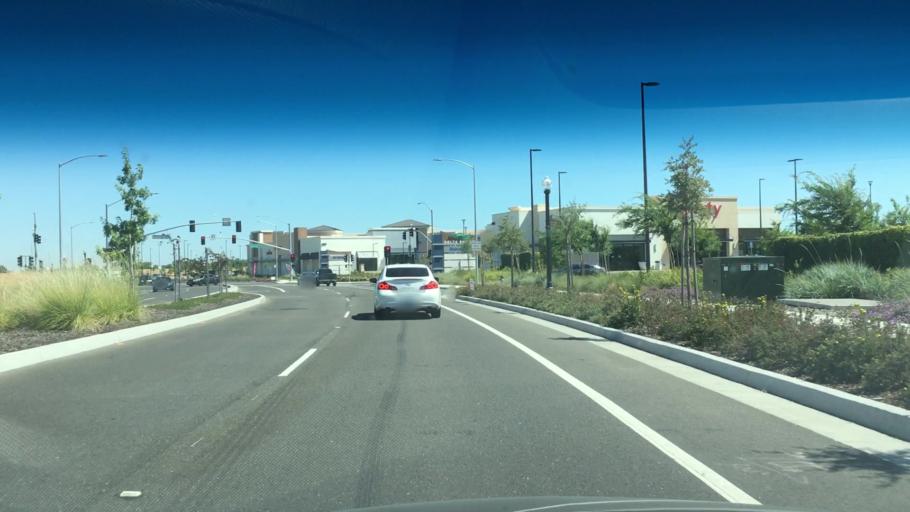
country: US
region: California
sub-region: Sacramento County
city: Parkway
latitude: 38.4610
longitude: -121.4907
